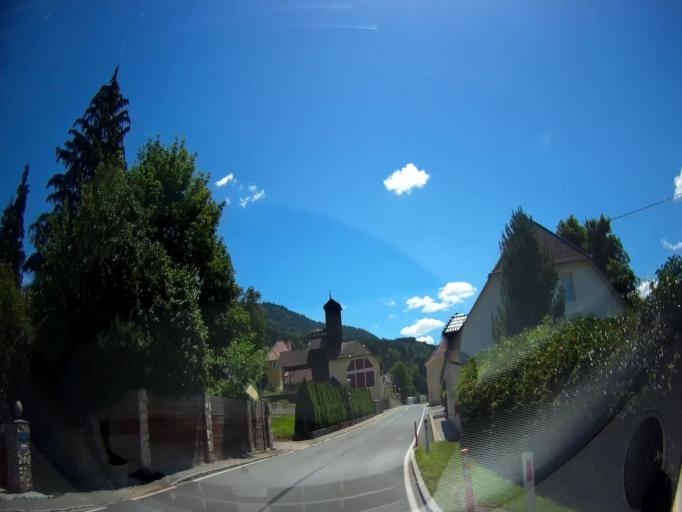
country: AT
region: Carinthia
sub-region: Politischer Bezirk Sankt Veit an der Glan
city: Sankt Veit an der Glan
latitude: 46.7380
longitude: 14.3928
